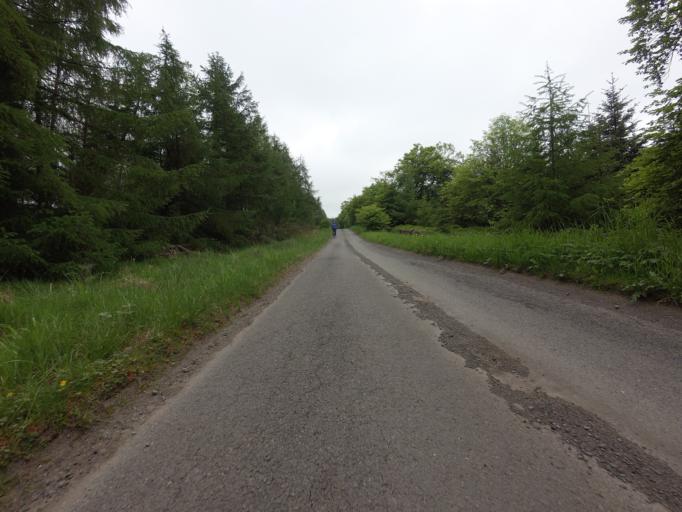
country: GB
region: Scotland
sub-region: Fife
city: Townhill
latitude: 56.1372
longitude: -3.4445
